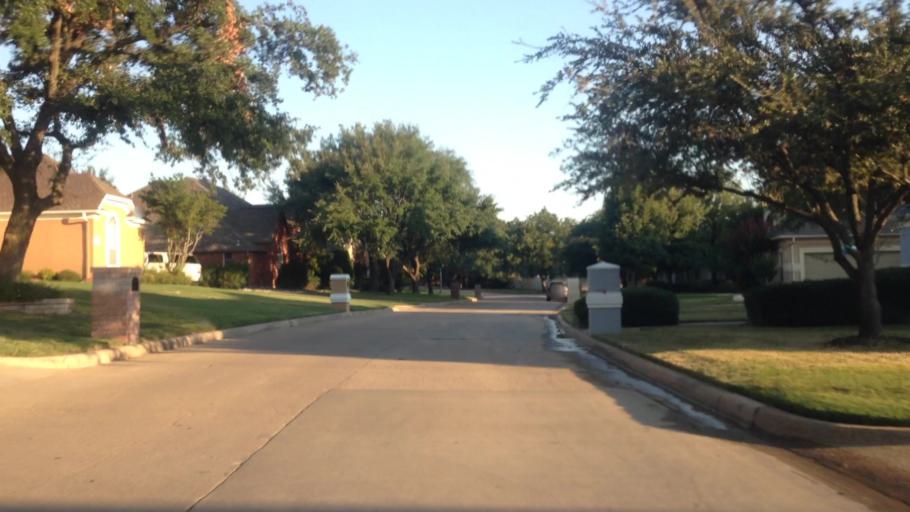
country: US
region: Texas
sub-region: Denton County
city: Trophy Club
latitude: 33.0028
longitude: -97.1687
